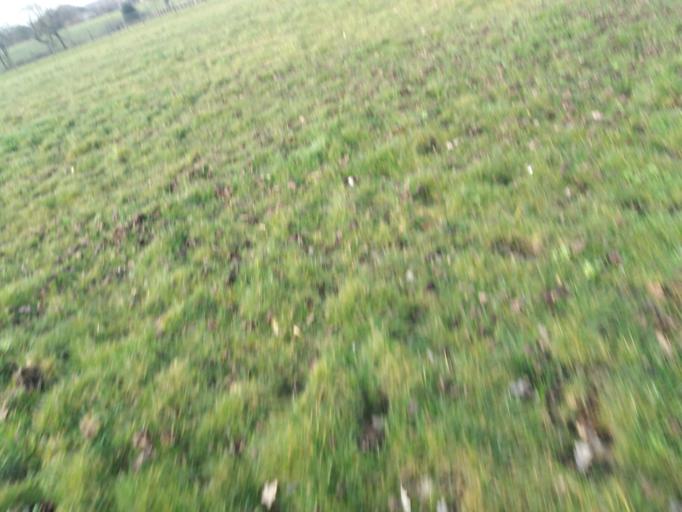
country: GB
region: England
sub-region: Lancashire
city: Coppull
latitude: 53.6451
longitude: -2.6701
